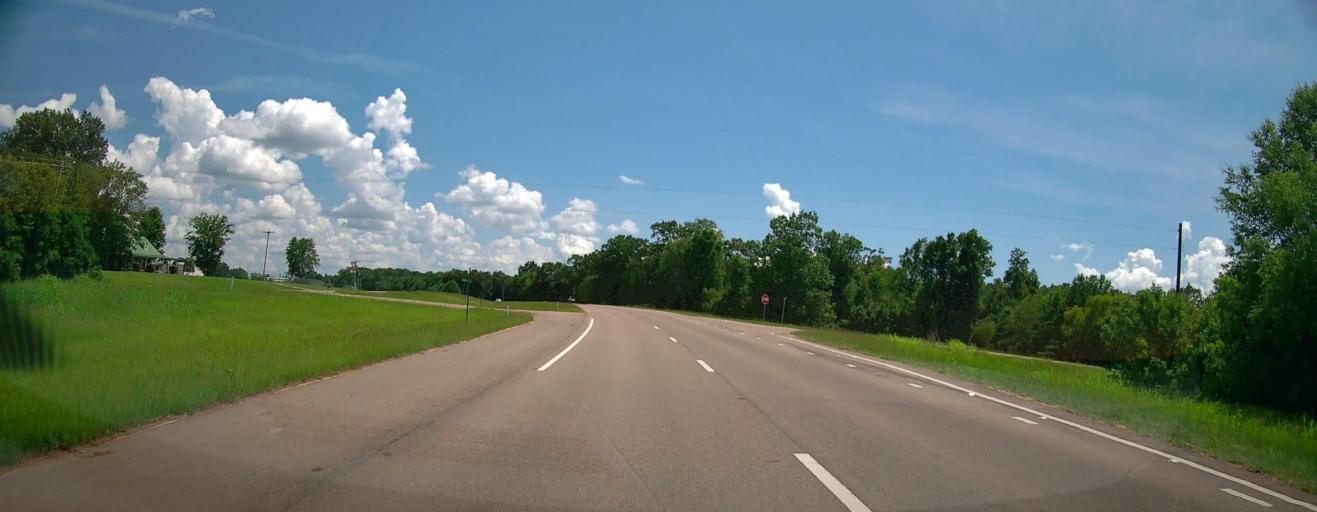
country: US
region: Mississippi
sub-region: Lee County
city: Nettleton
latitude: 33.9657
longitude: -88.6139
